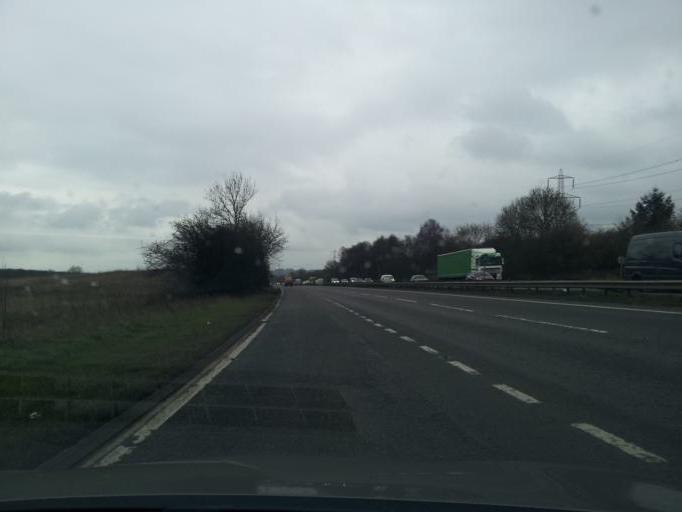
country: GB
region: England
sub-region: Lincolnshire
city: Barrowby
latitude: 52.9156
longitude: -0.6796
